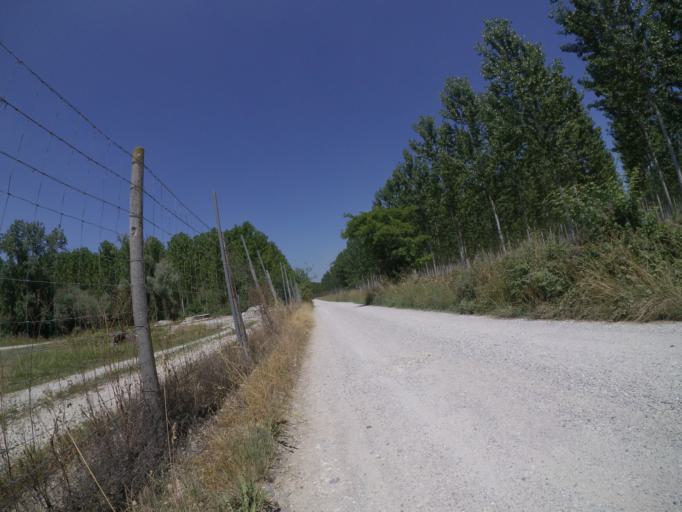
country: IT
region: Friuli Venezia Giulia
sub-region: Provincia di Udine
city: Rivignano
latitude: 45.9133
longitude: 13.0257
